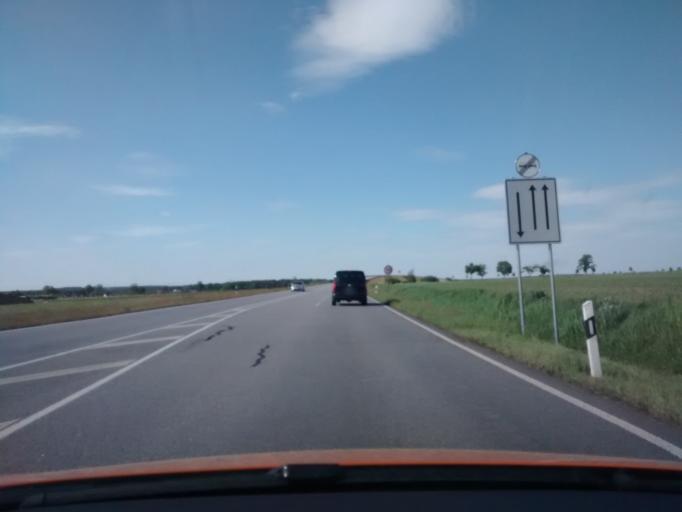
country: DE
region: Brandenburg
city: Luckenwalde
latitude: 52.1004
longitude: 13.1184
